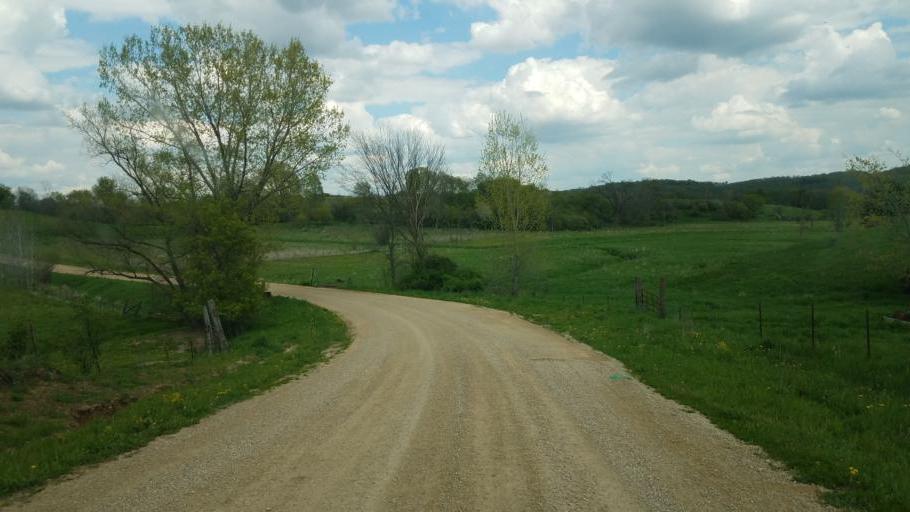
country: US
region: Wisconsin
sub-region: Vernon County
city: Hillsboro
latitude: 43.6297
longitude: -90.3756
